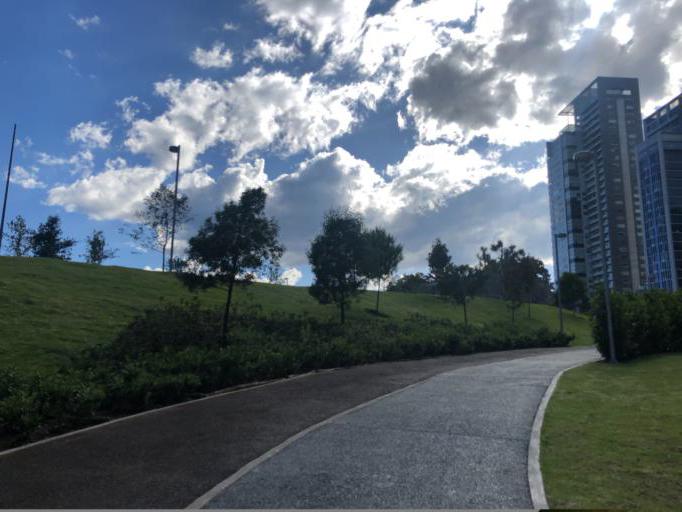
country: MX
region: Mexico City
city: Cuajimalpa
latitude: 19.3568
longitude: -99.2729
